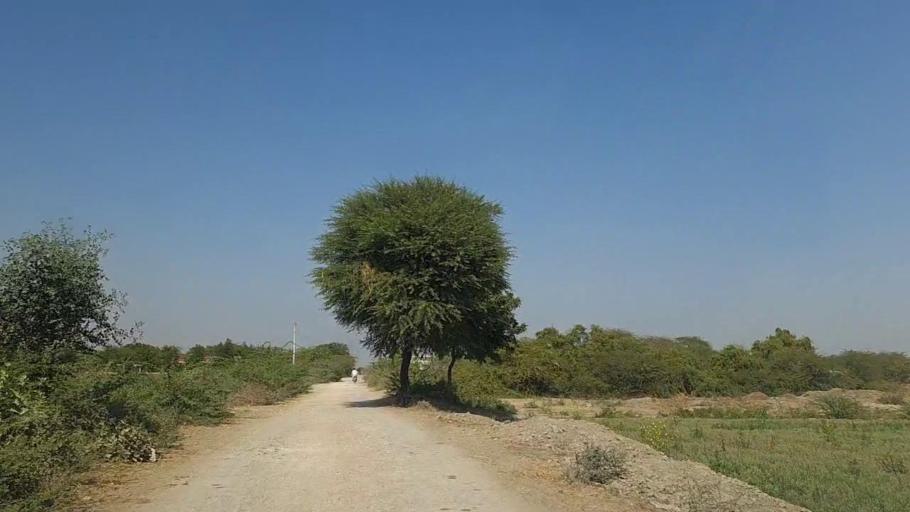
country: PK
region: Sindh
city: Naukot
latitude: 24.8720
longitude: 69.4038
